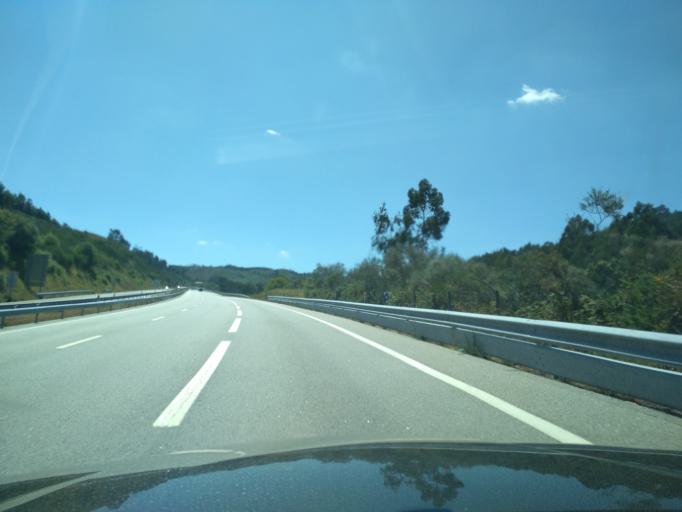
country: PT
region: Braga
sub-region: Cabeceiras de Basto
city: Refojos de Basto
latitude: 41.4536
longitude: -8.0431
